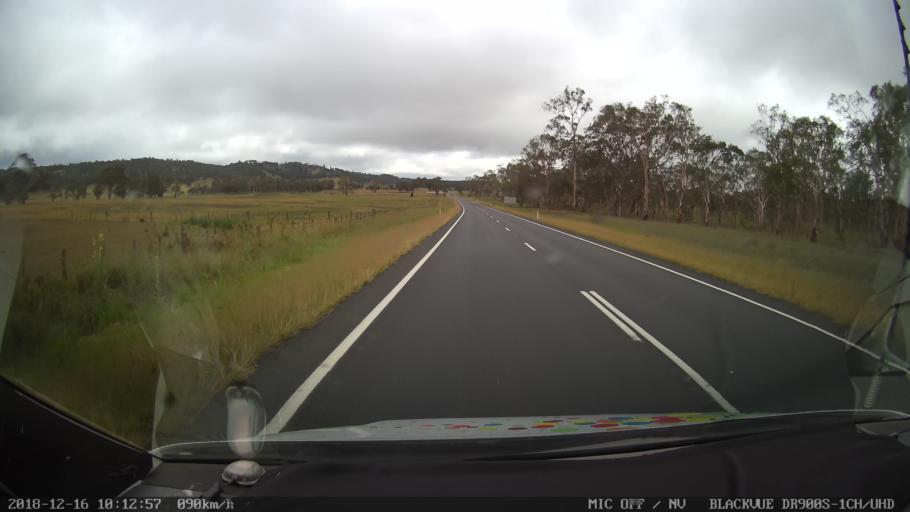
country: AU
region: New South Wales
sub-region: Glen Innes Severn
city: Glen Innes
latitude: -29.3017
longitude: 151.9470
